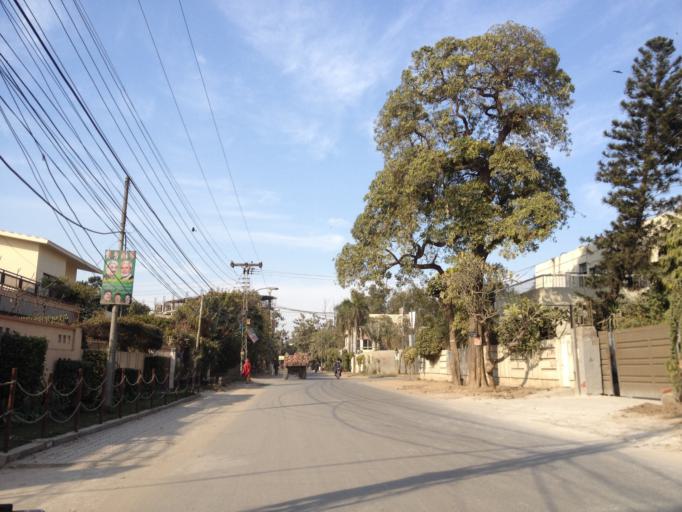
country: PK
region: Punjab
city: Lahore
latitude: 31.5042
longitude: 74.3189
